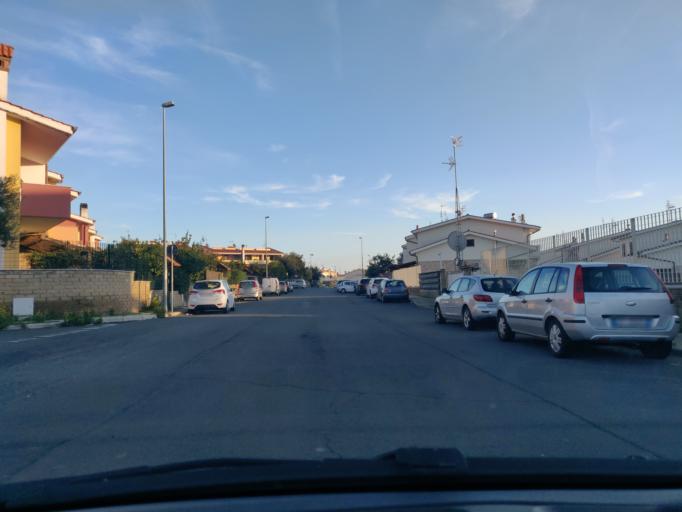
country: IT
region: Latium
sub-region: Citta metropolitana di Roma Capitale
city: Civitavecchia
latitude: 42.0649
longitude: 11.8173
